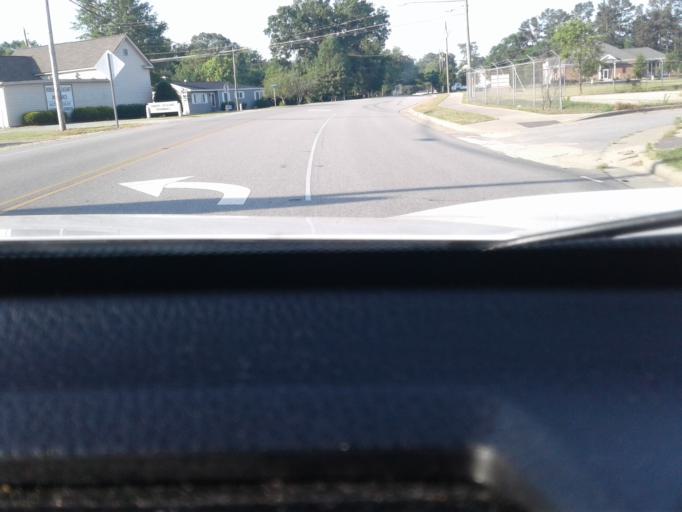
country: US
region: North Carolina
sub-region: Harnett County
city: Dunn
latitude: 35.3174
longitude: -78.6208
